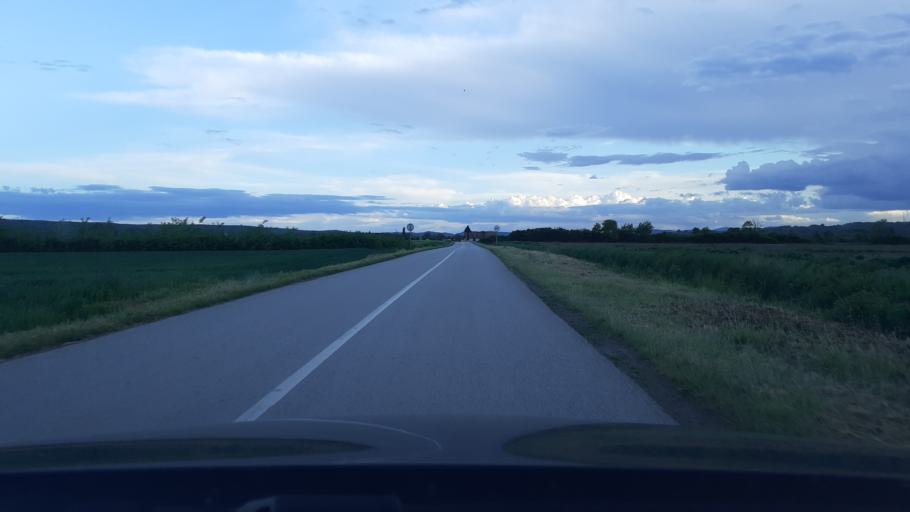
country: HR
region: Pozesko-Slavonska
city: Gradac
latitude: 45.3222
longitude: 17.8114
